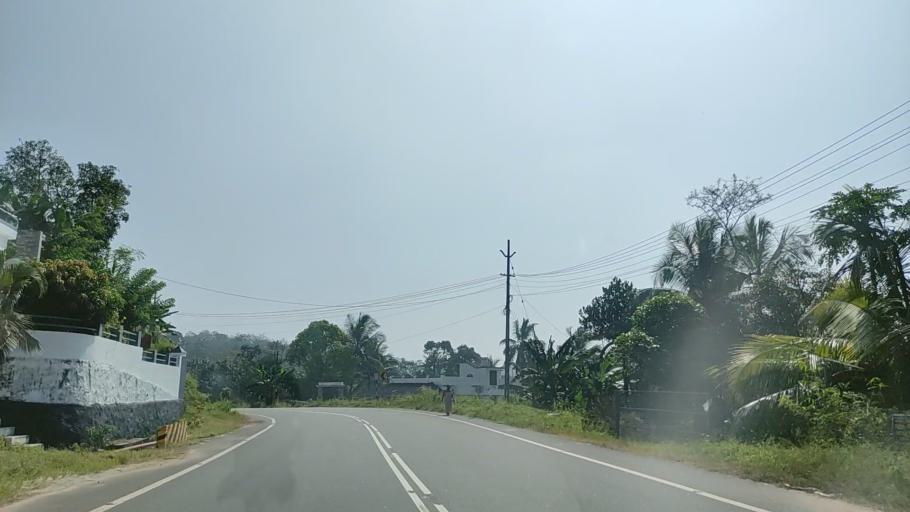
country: IN
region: Kerala
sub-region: Kollam
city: Punalur
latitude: 8.9304
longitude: 76.9930
